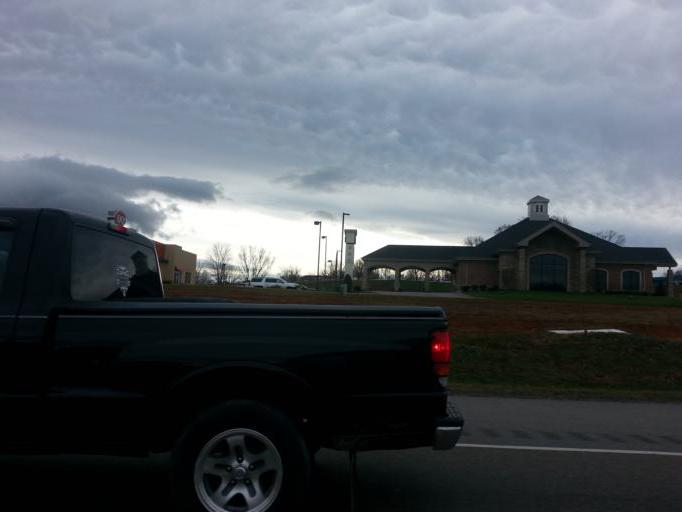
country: US
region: Tennessee
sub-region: Greene County
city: Tusculum
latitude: 36.1854
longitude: -82.7610
